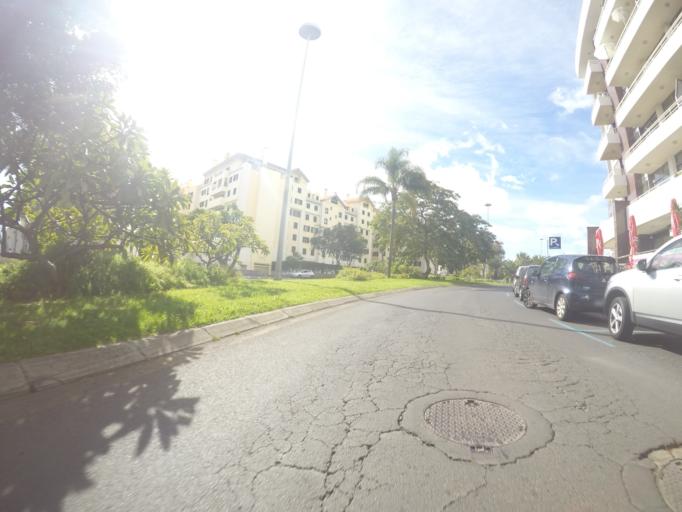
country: PT
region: Madeira
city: Camara de Lobos
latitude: 32.6359
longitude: -16.9407
